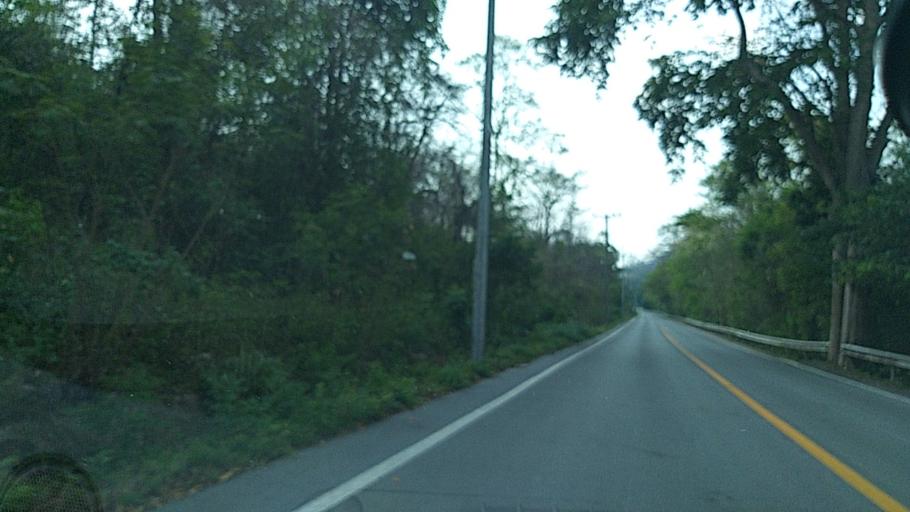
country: TH
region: Sara Buri
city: Saraburi
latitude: 14.4513
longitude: 100.9537
